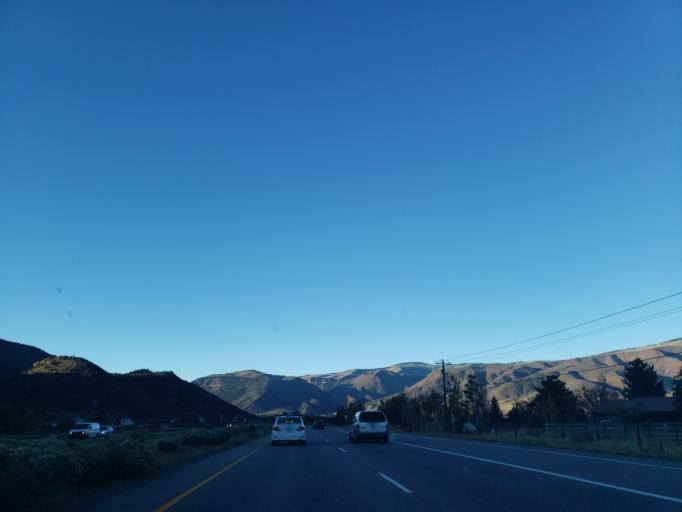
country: US
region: Colorado
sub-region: Pitkin County
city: Snowmass Village
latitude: 39.2535
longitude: -106.8850
